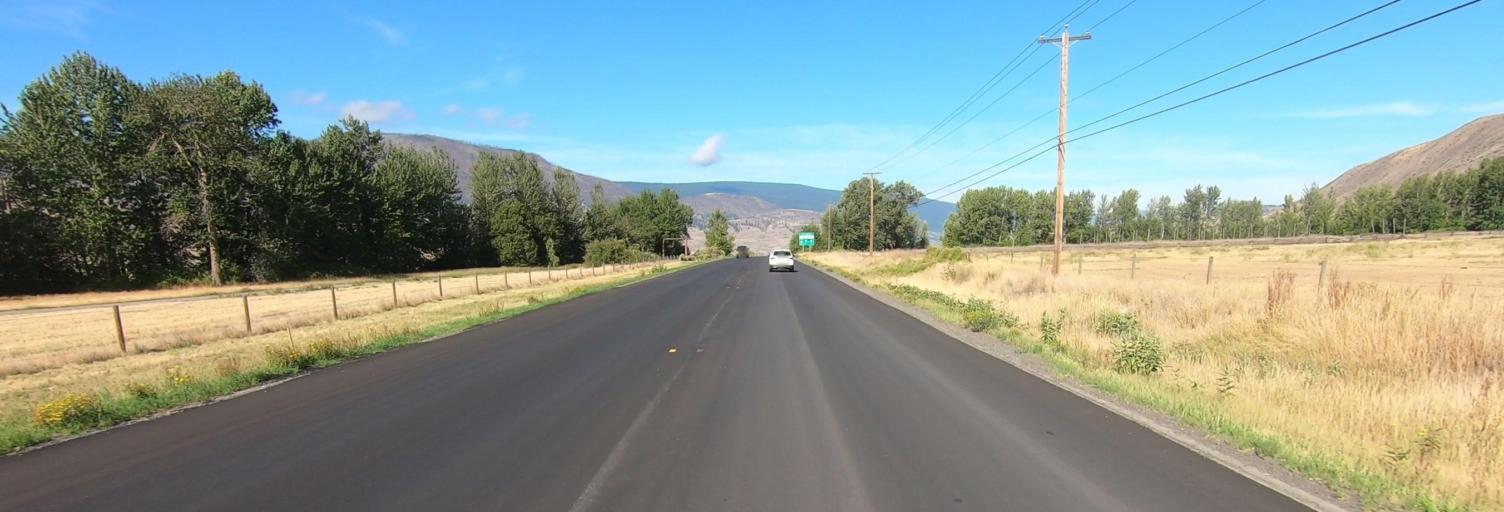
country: CA
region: British Columbia
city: Cache Creek
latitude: 50.8055
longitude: -121.2845
